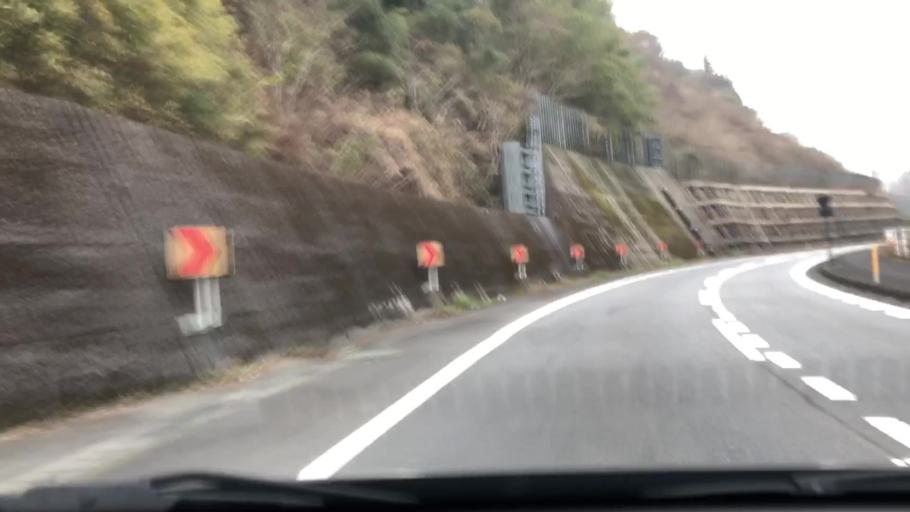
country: JP
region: Oita
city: Takedamachi
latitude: 32.9799
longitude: 131.5486
